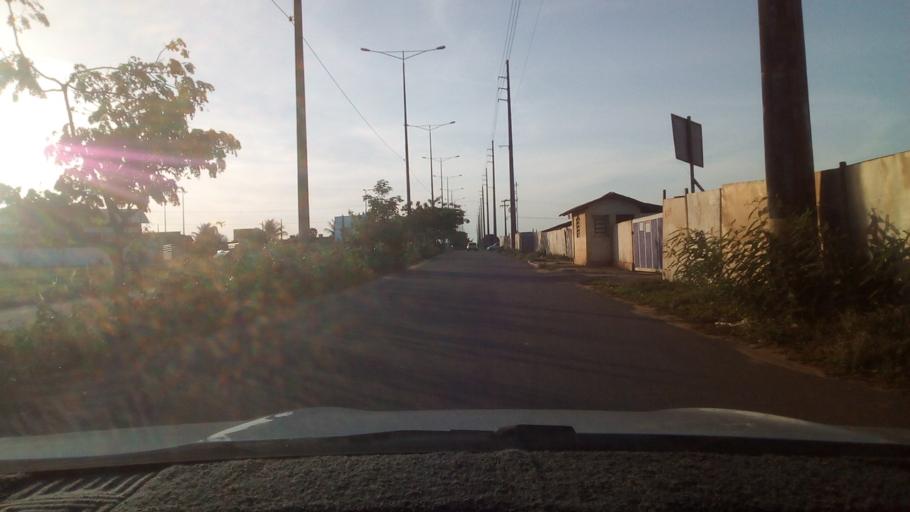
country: BR
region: Paraiba
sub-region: Conde
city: Conde
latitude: -7.1990
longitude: -34.8797
